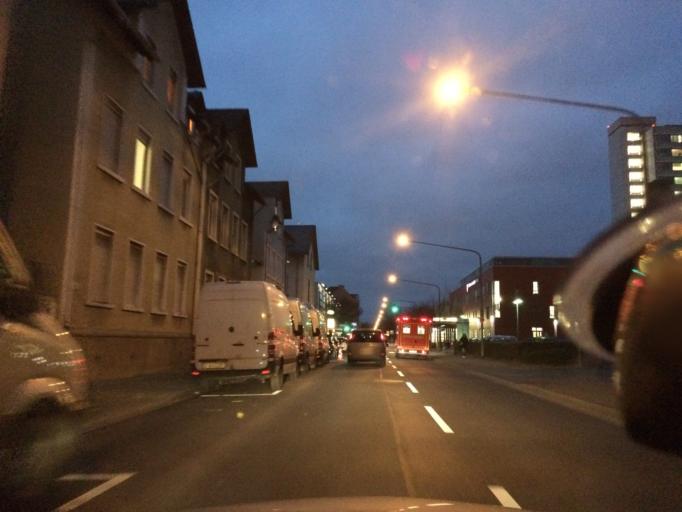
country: DE
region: Hesse
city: Sulzbach
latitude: 50.1068
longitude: 8.5449
